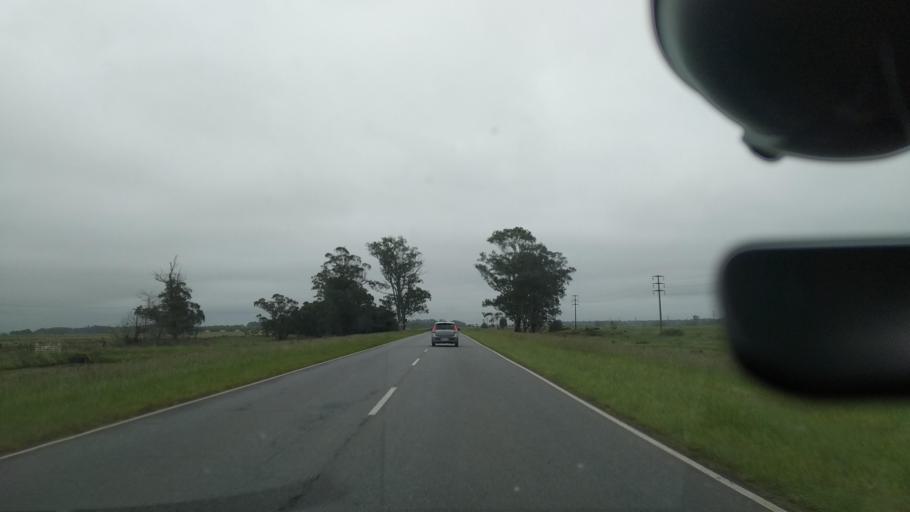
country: AR
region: Buenos Aires
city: Veronica
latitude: -35.3368
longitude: -57.4554
